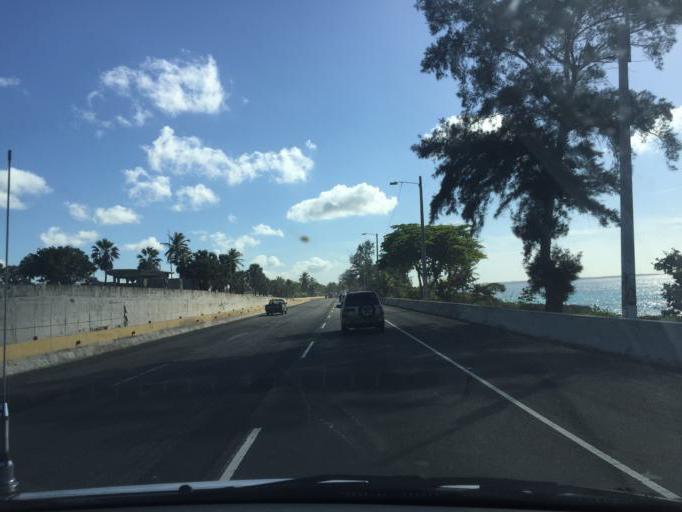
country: DO
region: Santo Domingo
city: Guerra
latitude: 18.4583
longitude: -69.7221
